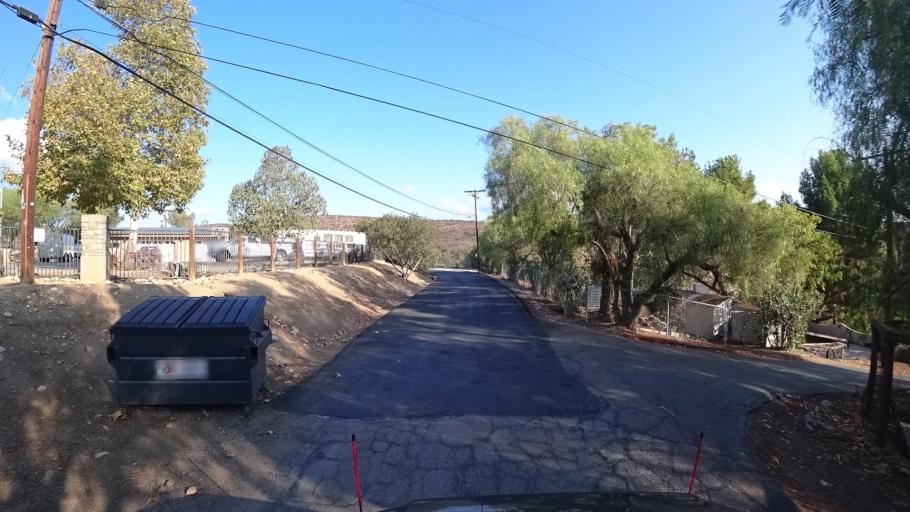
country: US
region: California
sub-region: San Diego County
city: Eucalyptus Hills
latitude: 32.8976
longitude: -116.9496
